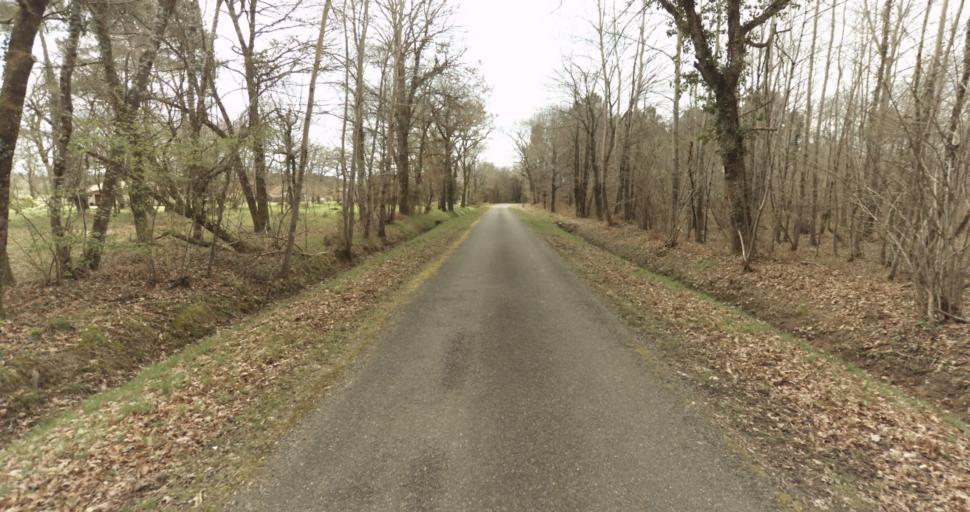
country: FR
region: Aquitaine
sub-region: Departement des Landes
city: Roquefort
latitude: 44.0728
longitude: -0.3933
